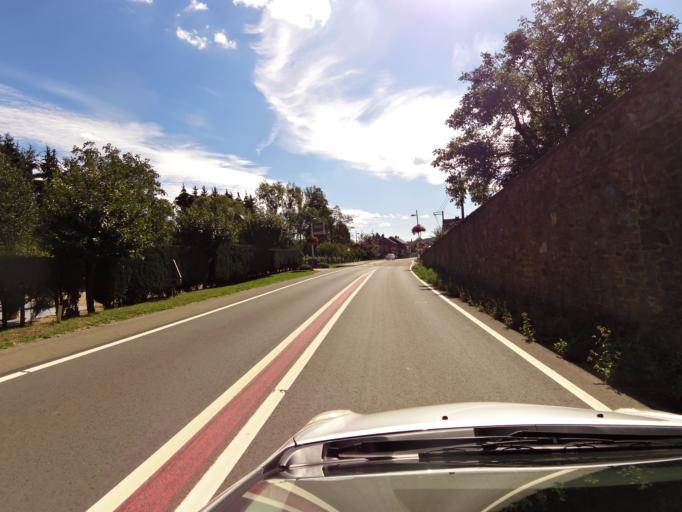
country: BE
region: Wallonia
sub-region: Province du Luxembourg
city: Rendeux
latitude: 50.2480
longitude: 5.4944
